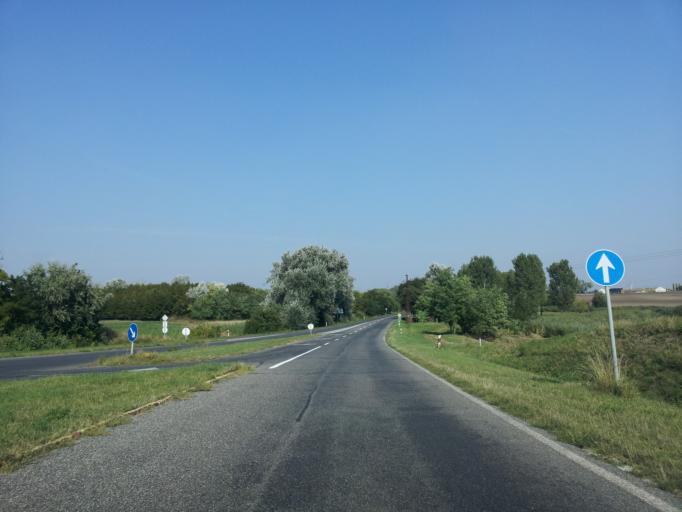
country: HU
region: Fejer
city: Lepseny
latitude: 46.9806
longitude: 18.2166
